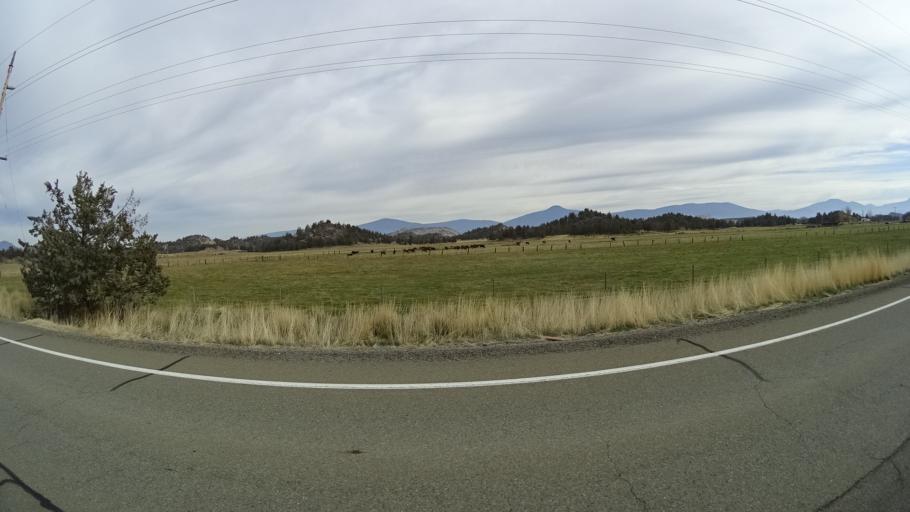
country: US
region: California
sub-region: Siskiyou County
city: Montague
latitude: 41.6753
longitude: -122.5260
